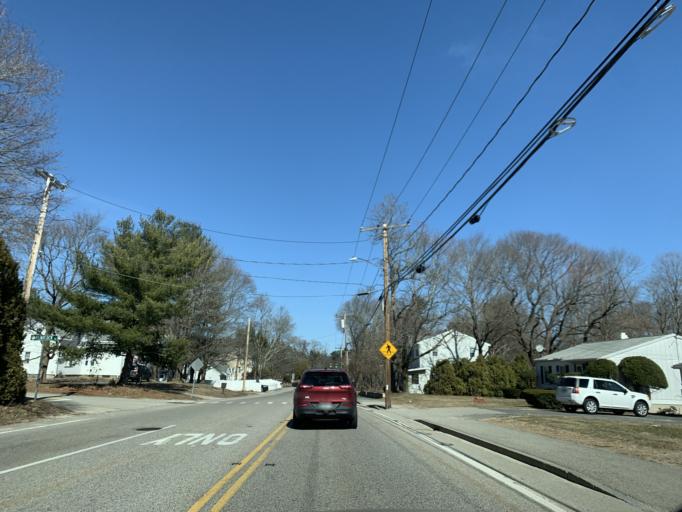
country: US
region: Massachusetts
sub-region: Norfolk County
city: Sharon
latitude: 42.1125
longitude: -71.1888
